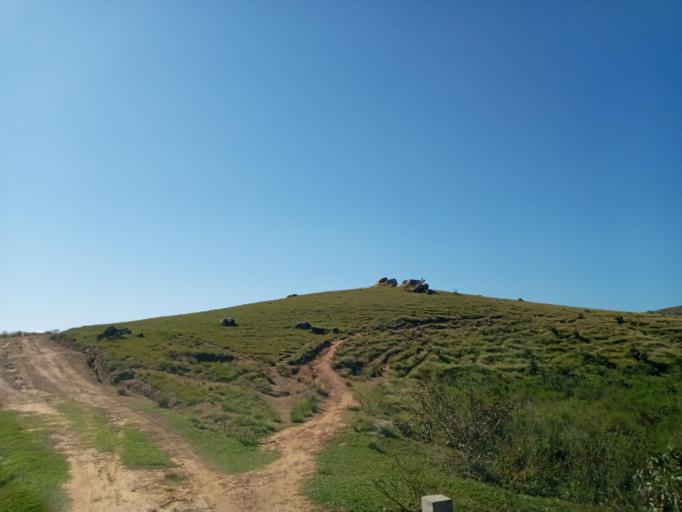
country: MG
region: Anosy
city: Fort Dauphin
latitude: -24.9103
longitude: 47.0727
